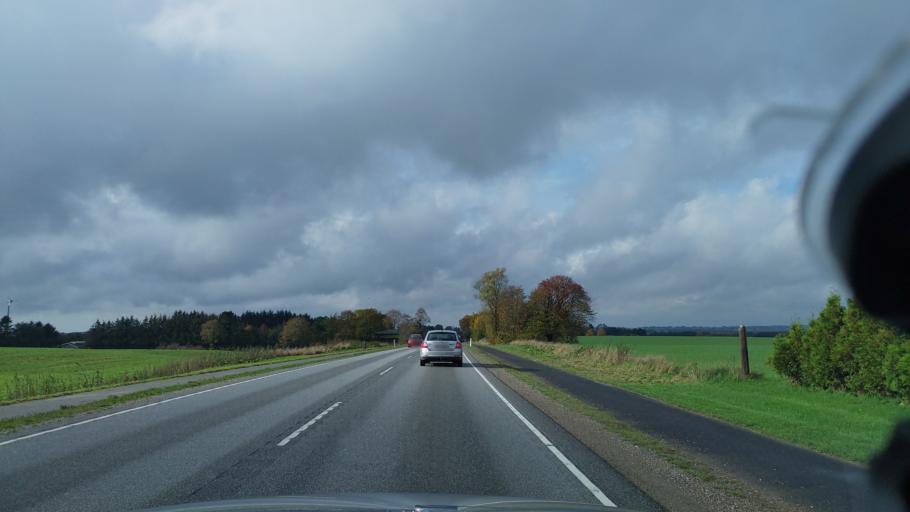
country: DK
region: Zealand
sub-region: Faxe Kommune
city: Haslev
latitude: 55.2586
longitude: 11.9005
